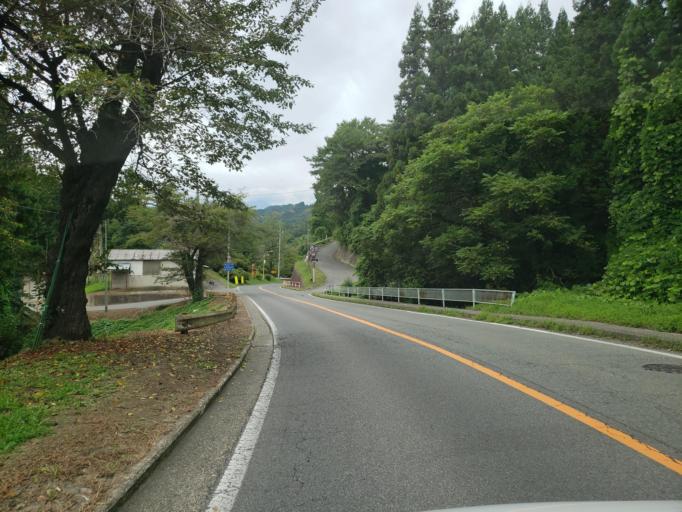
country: JP
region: Nagano
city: Nagano-shi
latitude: 36.6125
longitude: 138.0586
